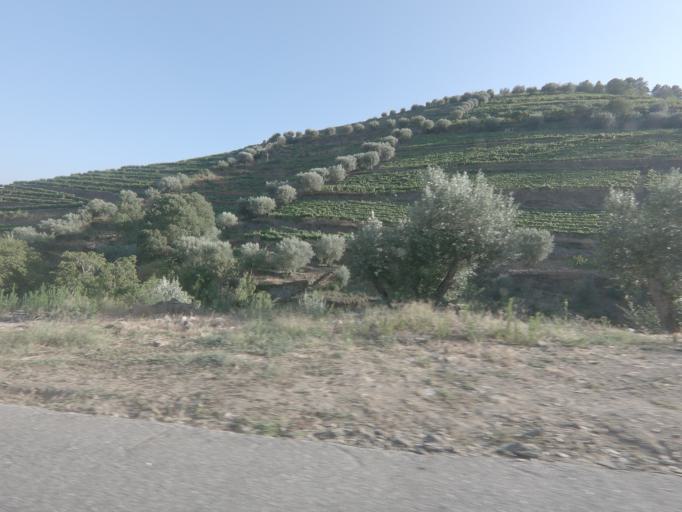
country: PT
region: Vila Real
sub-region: Sabrosa
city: Vilela
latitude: 41.1821
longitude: -7.5828
